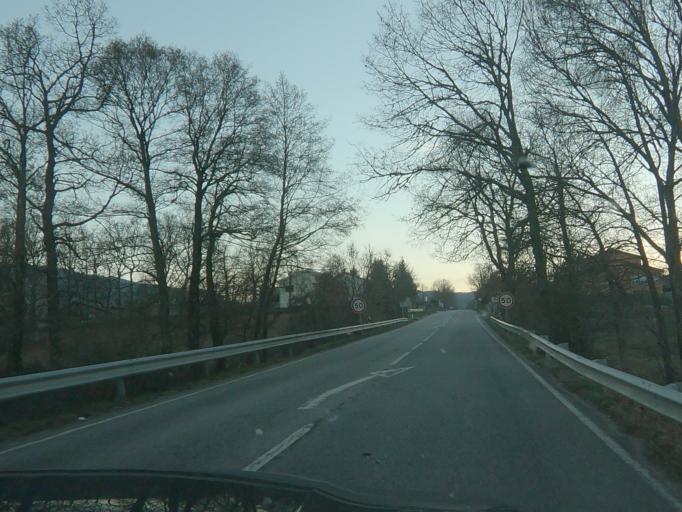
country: PT
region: Vila Real
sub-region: Vila Pouca de Aguiar
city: Vila Pouca de Aguiar
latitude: 41.4331
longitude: -7.6791
